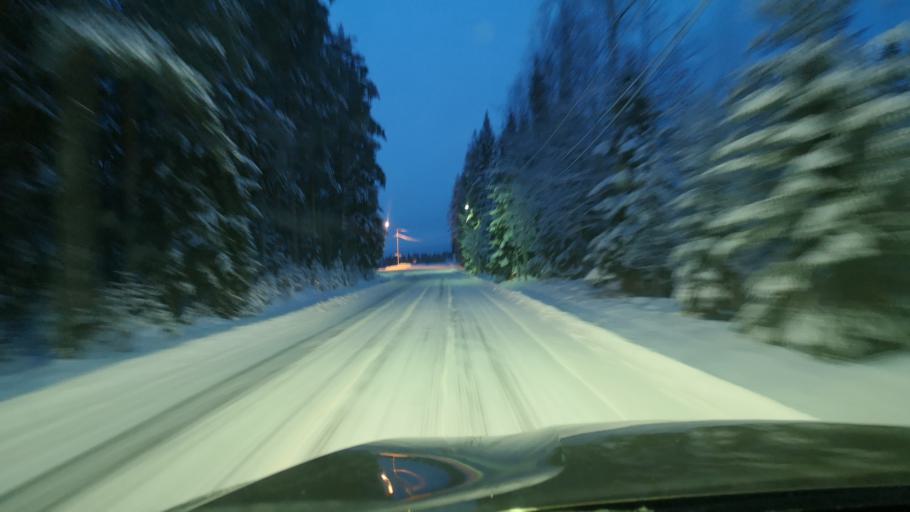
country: FI
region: Varsinais-Suomi
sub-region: Loimaa
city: Loimaa
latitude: 60.8693
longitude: 23.0887
